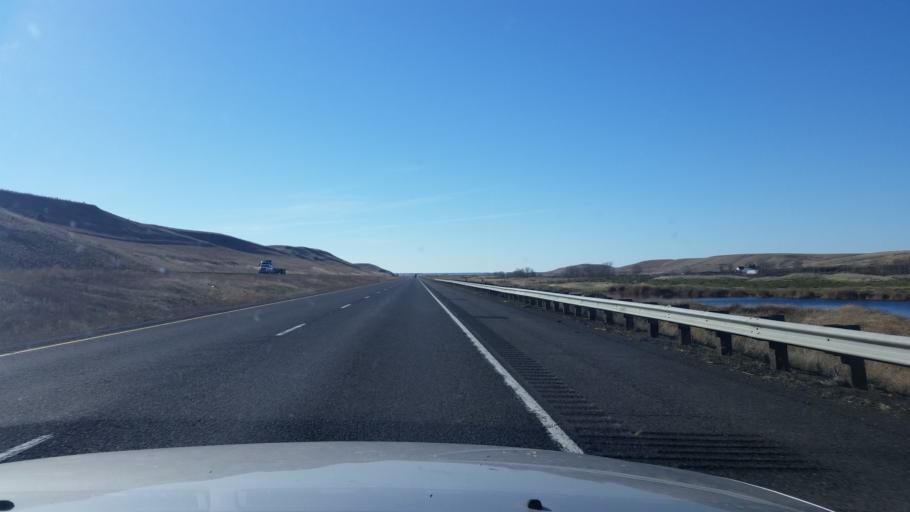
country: US
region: Washington
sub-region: Spokane County
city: Medical Lake
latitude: 47.3627
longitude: -117.8874
